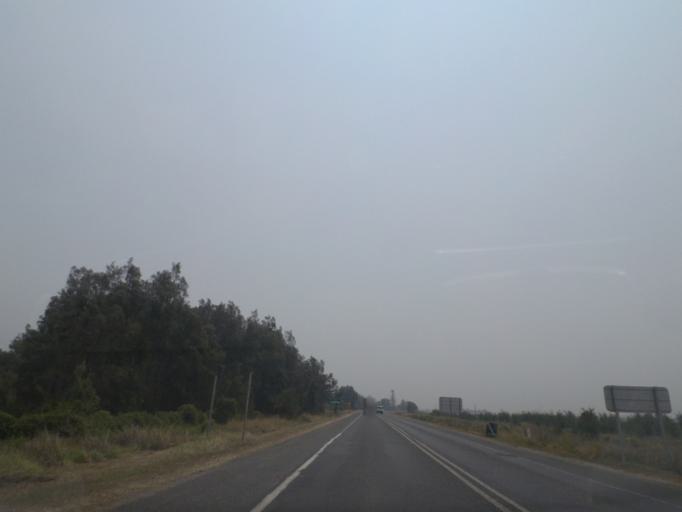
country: AU
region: New South Wales
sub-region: Clarence Valley
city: Maclean
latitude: -29.4224
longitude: 153.2411
